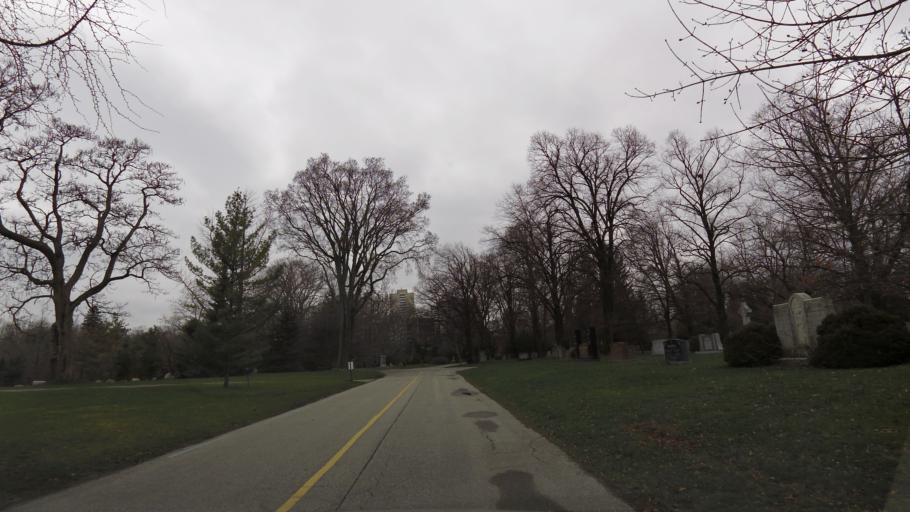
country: CA
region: Ontario
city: Toronto
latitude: 43.6968
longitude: -79.3822
